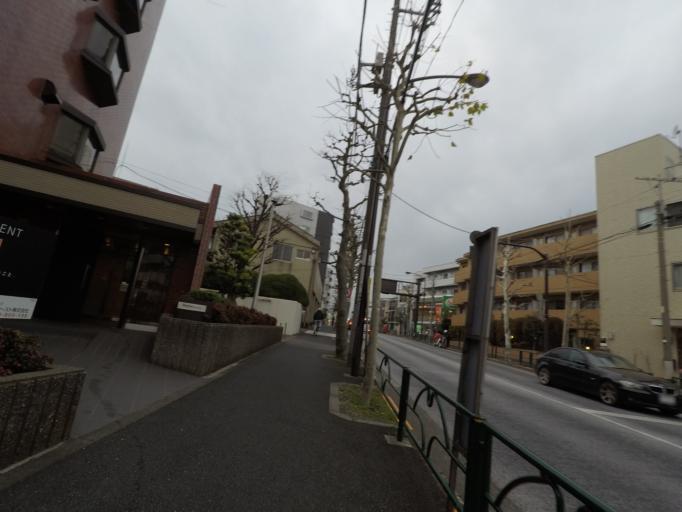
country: JP
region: Tokyo
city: Tokyo
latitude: 35.7229
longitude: 139.6804
